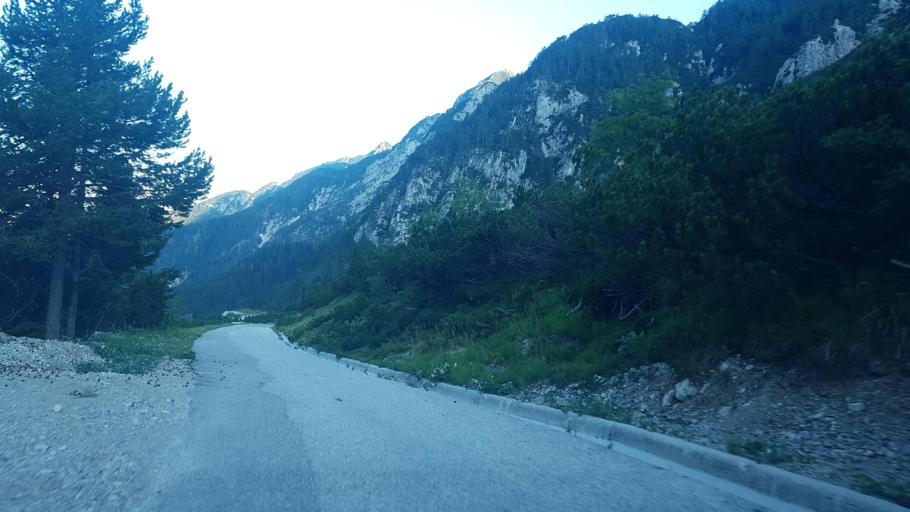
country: IT
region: Friuli Venezia Giulia
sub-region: Provincia di Udine
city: Malborghetto
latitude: 46.4633
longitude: 13.4369
